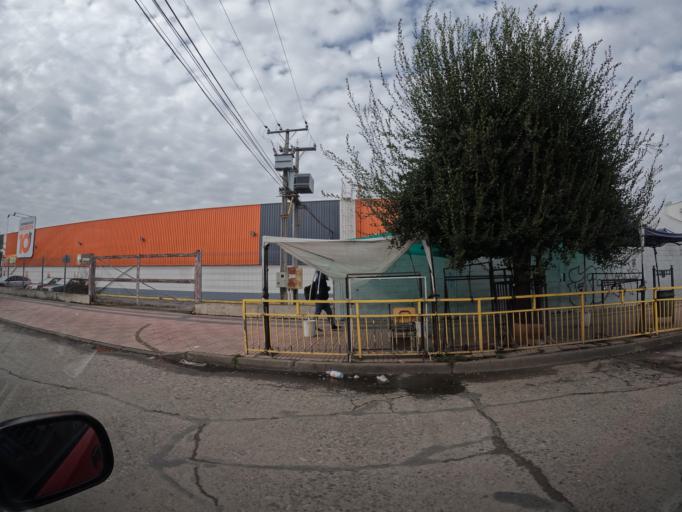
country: CL
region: Maule
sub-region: Provincia de Linares
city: Linares
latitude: -35.8461
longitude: -71.5908
